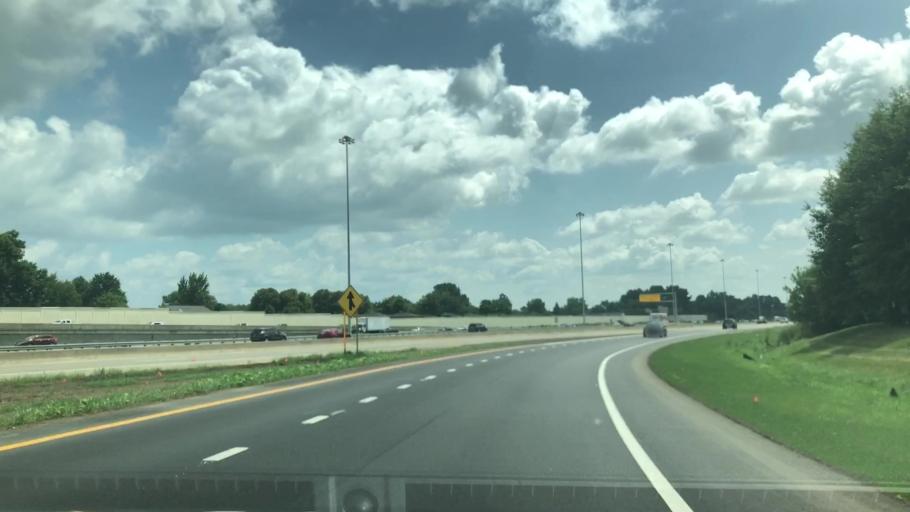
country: US
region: Ohio
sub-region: Franklin County
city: Gahanna
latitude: 40.0463
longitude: -82.9031
